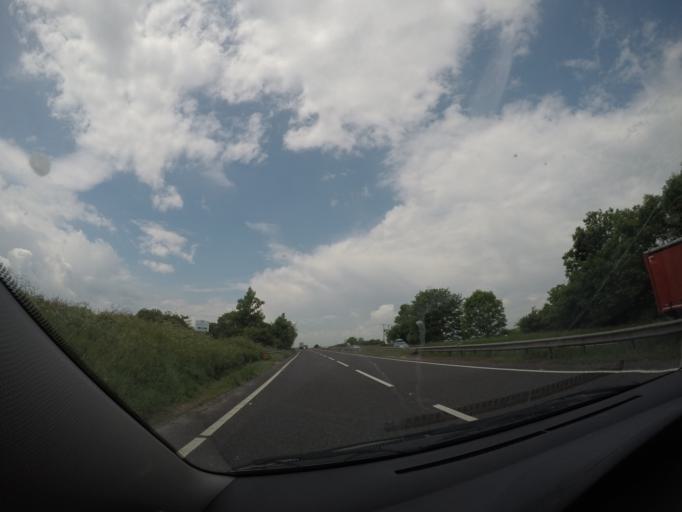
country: GB
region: England
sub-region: County Durham
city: Rokeby
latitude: 54.5044
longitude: -1.8444
